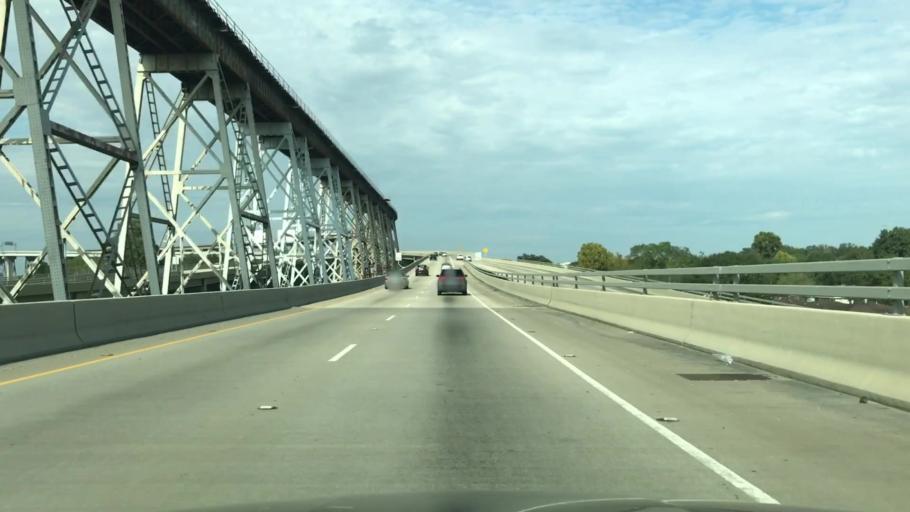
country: US
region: Louisiana
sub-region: Jefferson Parish
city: Bridge City
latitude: 29.9323
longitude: -90.1643
